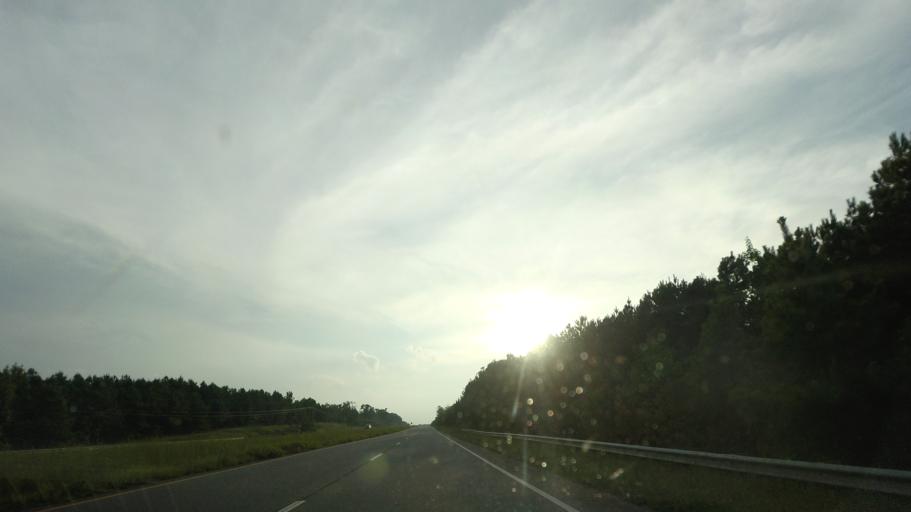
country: US
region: Georgia
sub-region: Wilkinson County
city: Gordon
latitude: 32.8519
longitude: -83.4056
